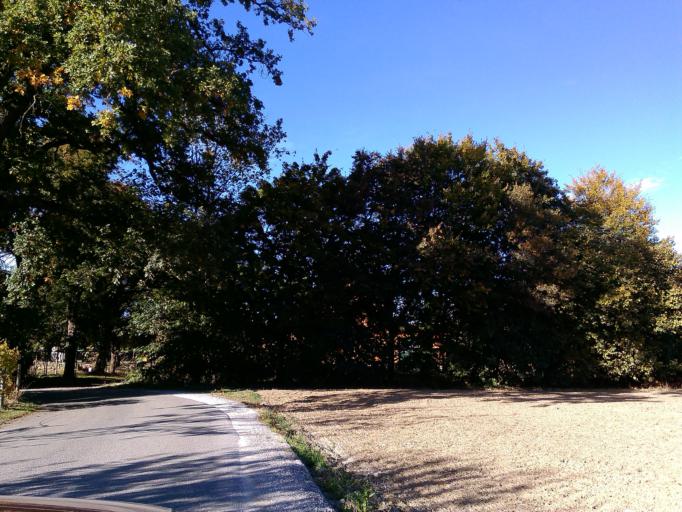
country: DE
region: Bavaria
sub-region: Upper Bavaria
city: Starnberg
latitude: 48.0424
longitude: 11.3326
